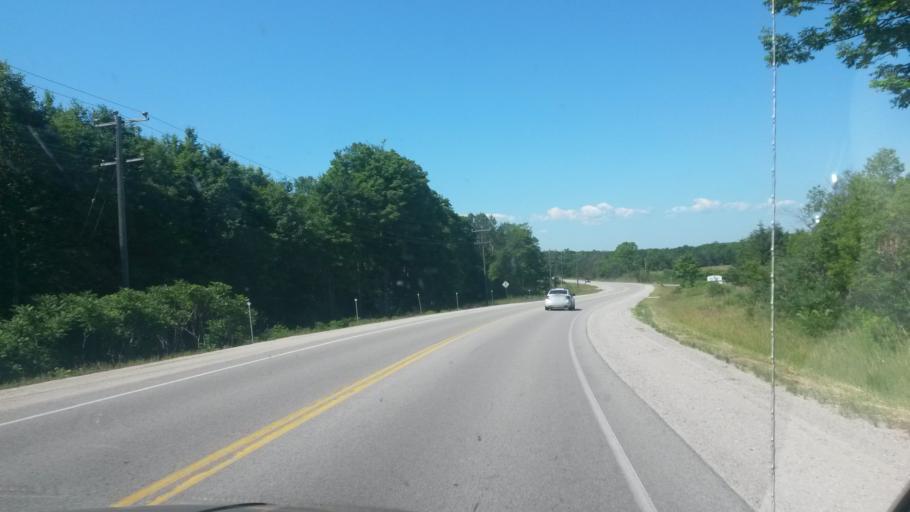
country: CA
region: Ontario
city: Barrie
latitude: 44.5410
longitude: -79.6996
